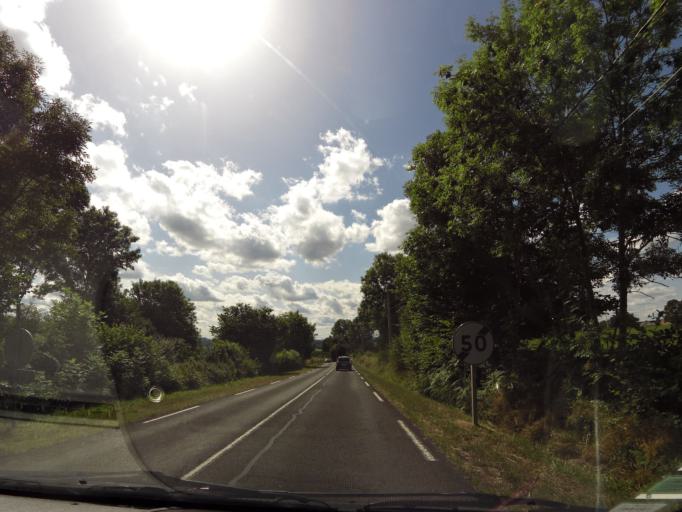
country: FR
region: Auvergne
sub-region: Departement du Puy-de-Dome
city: Aydat
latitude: 45.7294
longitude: 2.9031
